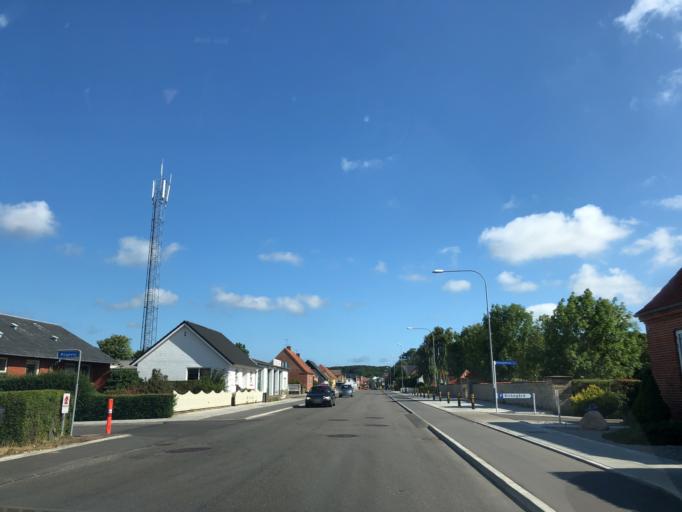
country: DK
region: North Denmark
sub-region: Jammerbugt Kommune
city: Fjerritslev
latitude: 57.0827
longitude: 9.2646
